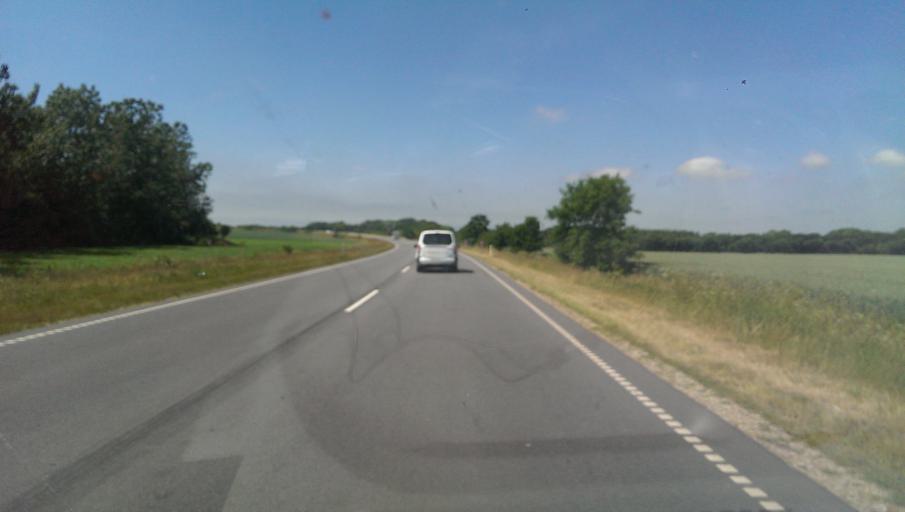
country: DK
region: South Denmark
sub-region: Esbjerg Kommune
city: Esbjerg
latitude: 55.5147
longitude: 8.4956
